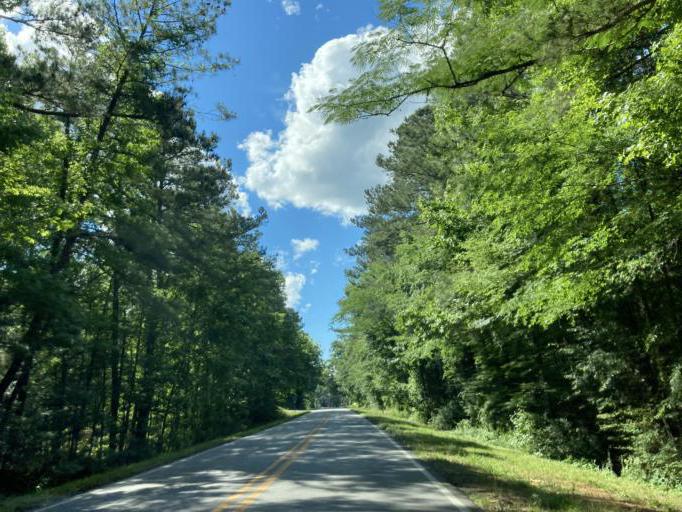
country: US
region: Georgia
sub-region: Jones County
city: Gray
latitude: 32.9962
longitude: -83.5526
